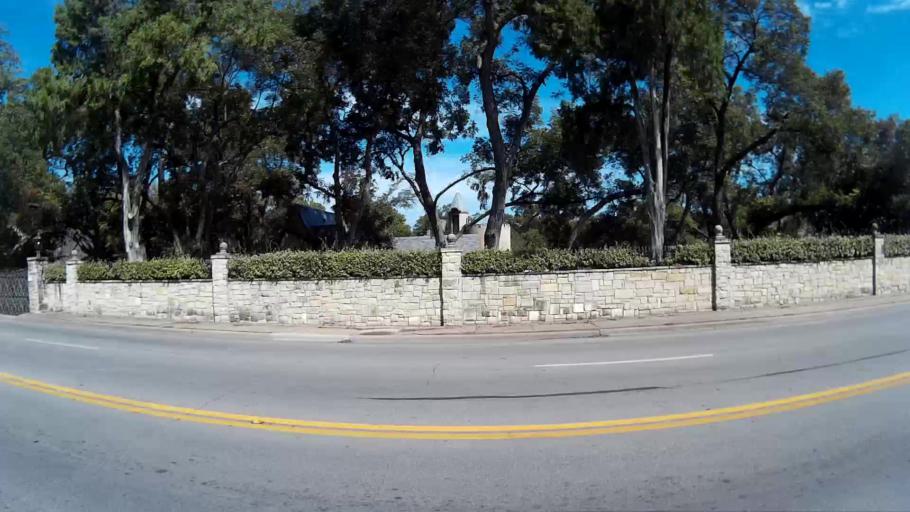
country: US
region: Texas
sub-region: Dallas County
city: Highland Park
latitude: 32.8153
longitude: -96.7381
